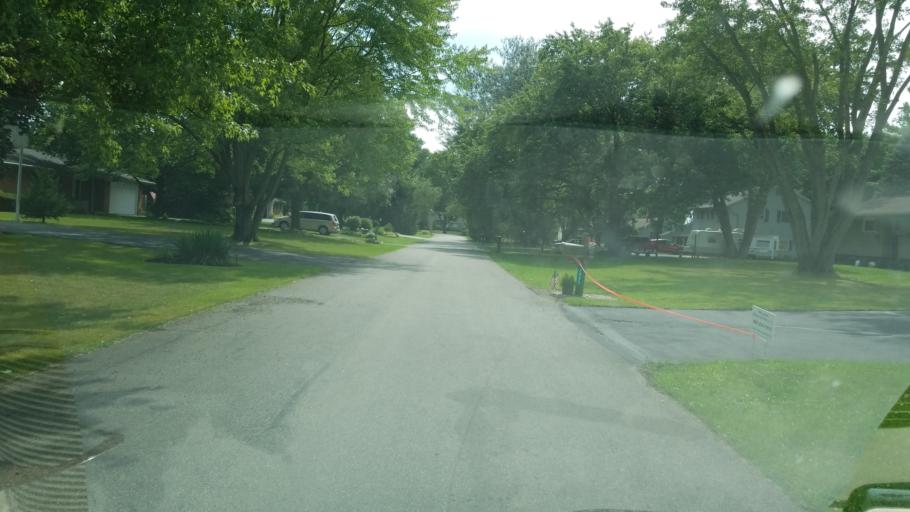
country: US
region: Ohio
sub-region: Marion County
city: Marion
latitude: 40.5326
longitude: -83.0945
